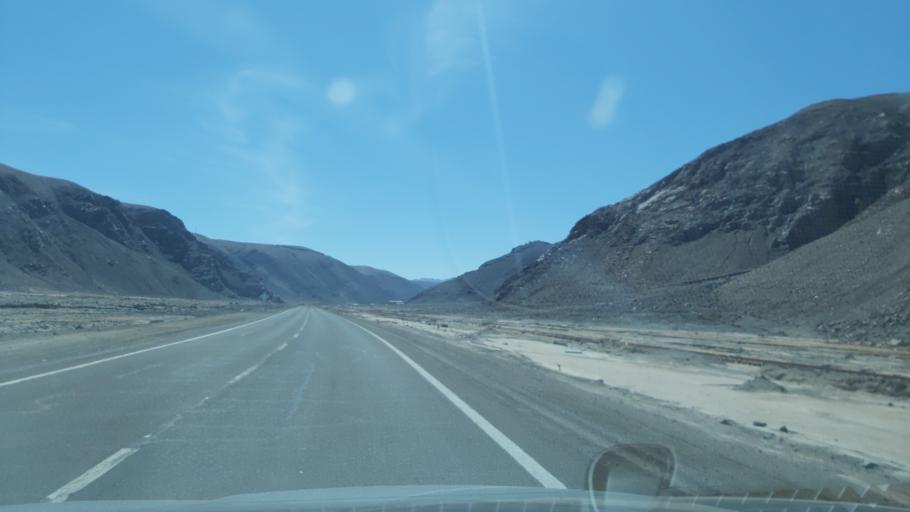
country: CL
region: Atacama
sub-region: Provincia de Chanaral
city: Diego de Almagro
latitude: -26.3423
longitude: -69.8403
